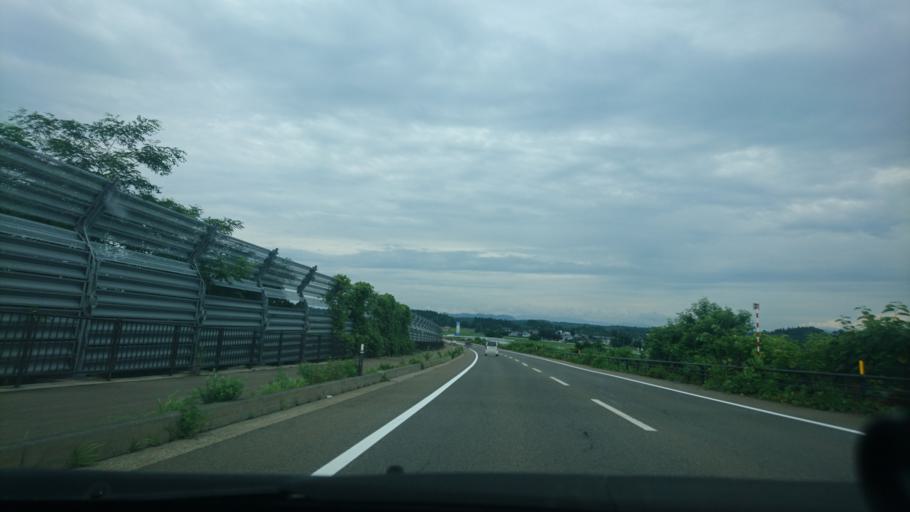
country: JP
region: Akita
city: Omagari
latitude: 39.4930
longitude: 140.4503
